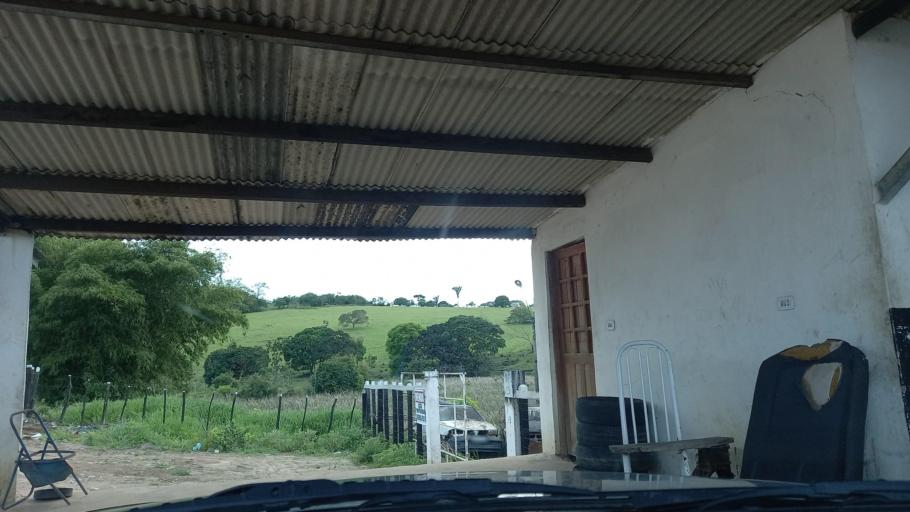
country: BR
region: Pernambuco
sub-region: Quipapa
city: Quipapa
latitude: -8.7863
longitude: -35.9599
